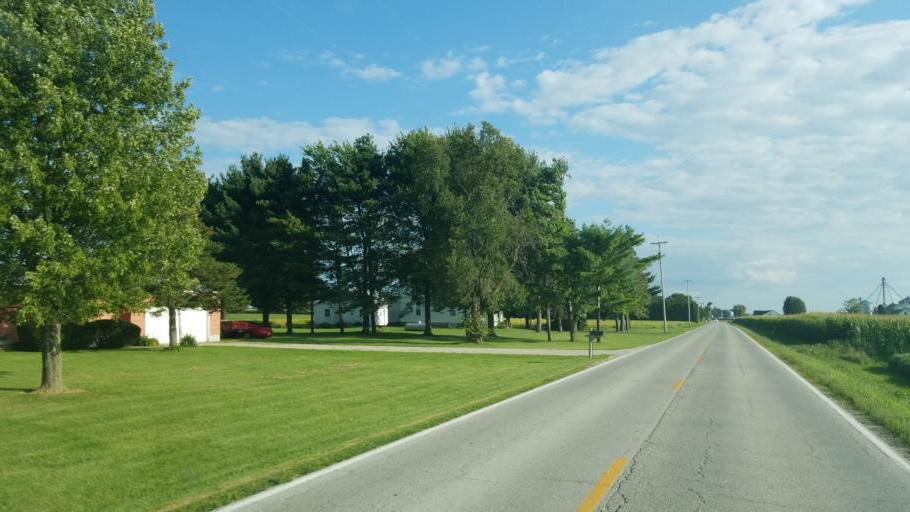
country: US
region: Ohio
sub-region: Sandusky County
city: Ballville
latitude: 41.2604
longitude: -83.1314
